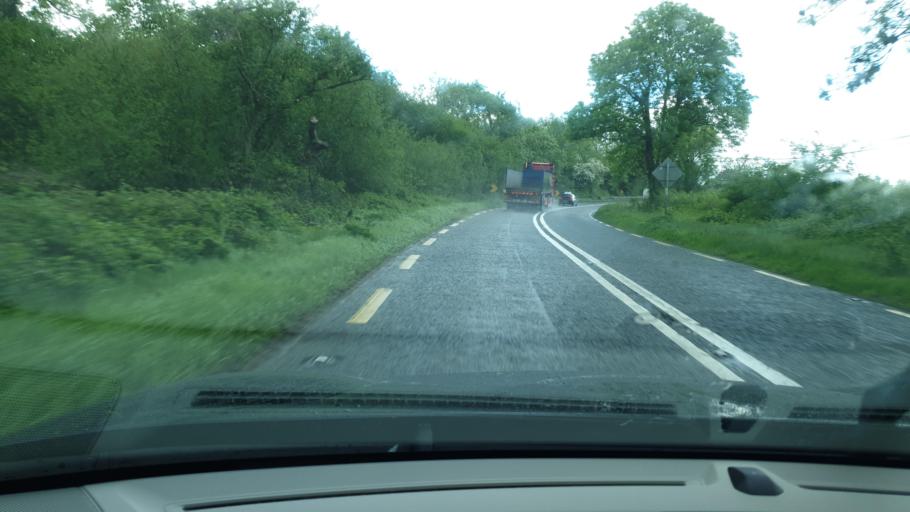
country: IE
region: Leinster
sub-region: Laois
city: Mountmellick
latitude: 53.1539
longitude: -7.3699
